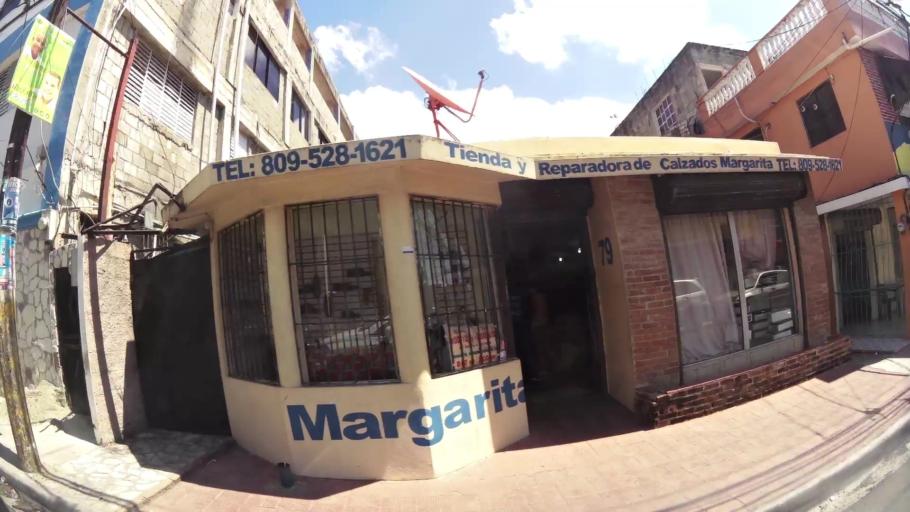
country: DO
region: San Cristobal
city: San Cristobal
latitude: 18.4151
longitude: -70.1090
